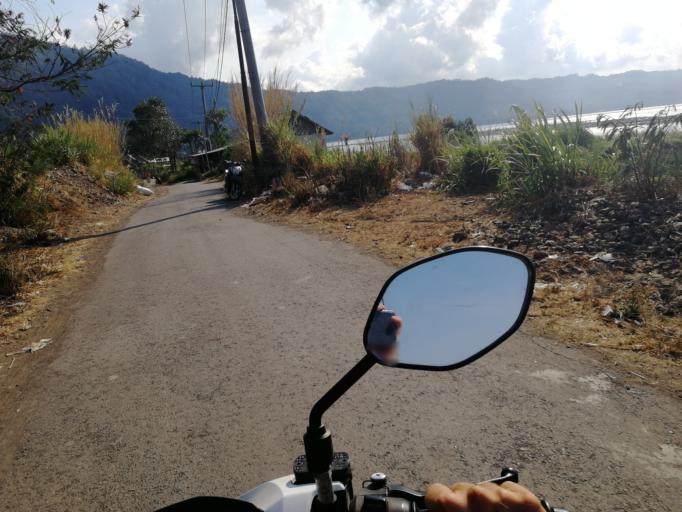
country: ID
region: Bali
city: Banjar Trunyan
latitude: -8.2724
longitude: 115.4140
